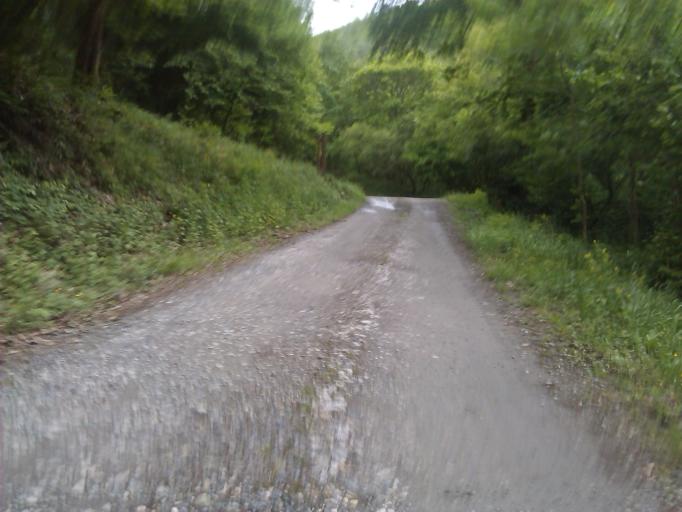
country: ES
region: Basque Country
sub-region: Provincia de Guipuzcoa
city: Berastegui
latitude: 43.1290
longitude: -1.9389
